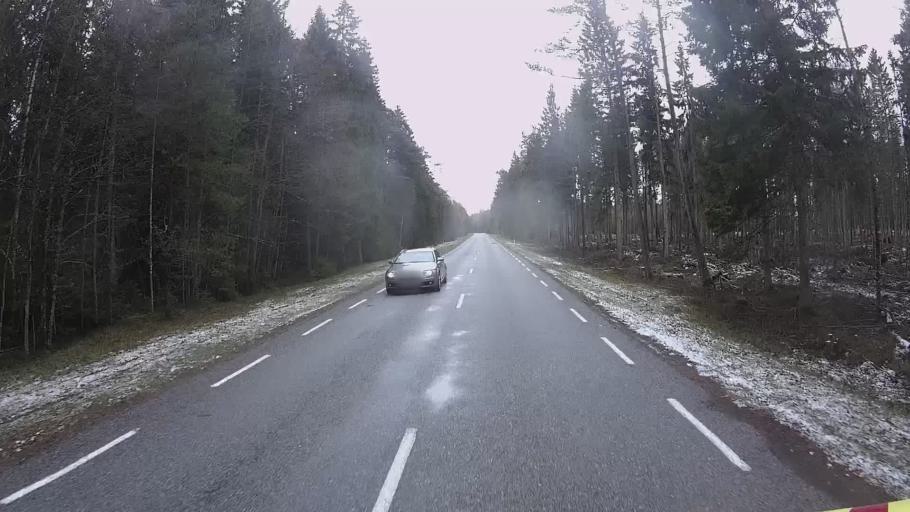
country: EE
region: Hiiumaa
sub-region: Kaerdla linn
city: Kardla
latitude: 59.0463
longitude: 22.6813
